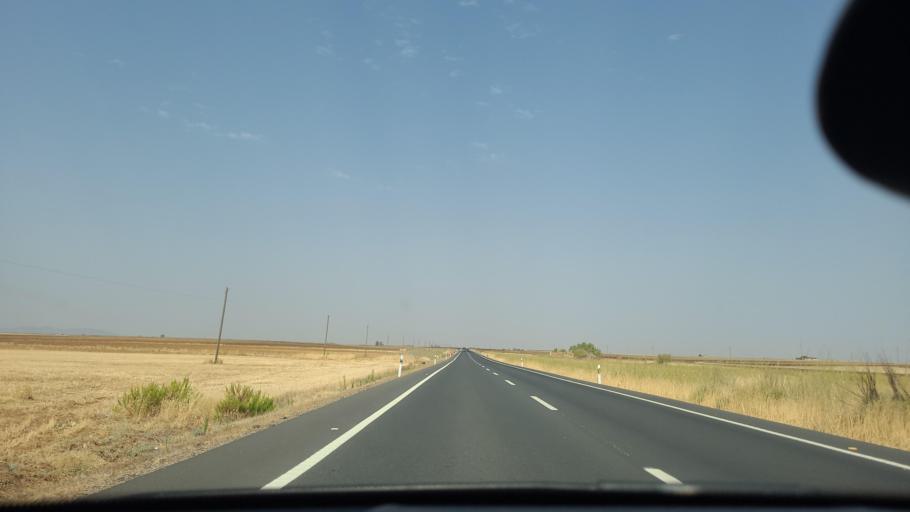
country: ES
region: Extremadura
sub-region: Provincia de Badajoz
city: Azuaga
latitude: 38.2609
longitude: -5.7256
